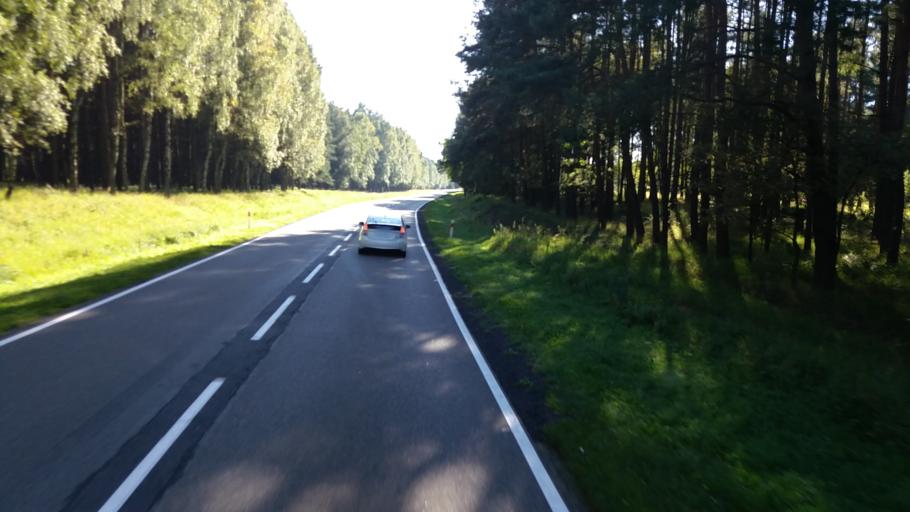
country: PL
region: West Pomeranian Voivodeship
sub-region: Powiat choszczenski
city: Drawno
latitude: 53.2954
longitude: 15.7366
